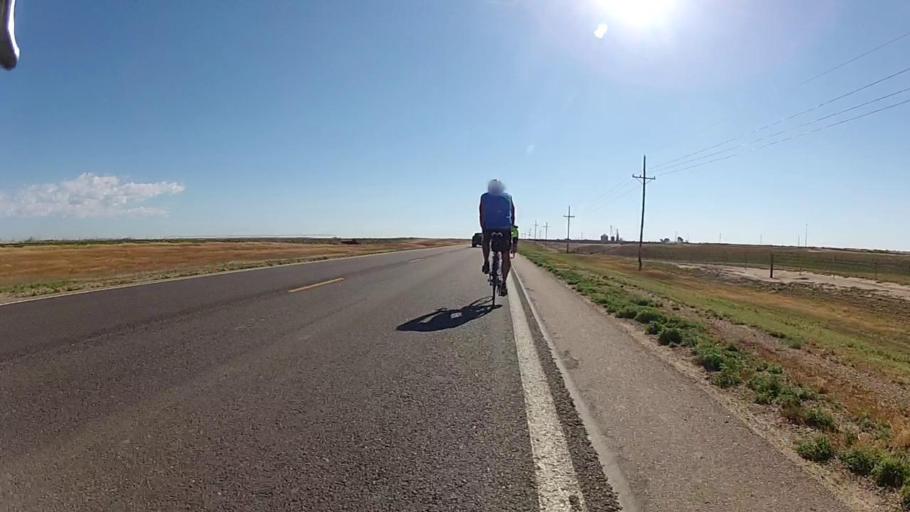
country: US
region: Kansas
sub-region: Gray County
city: Cimarron
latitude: 37.5697
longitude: -100.5424
